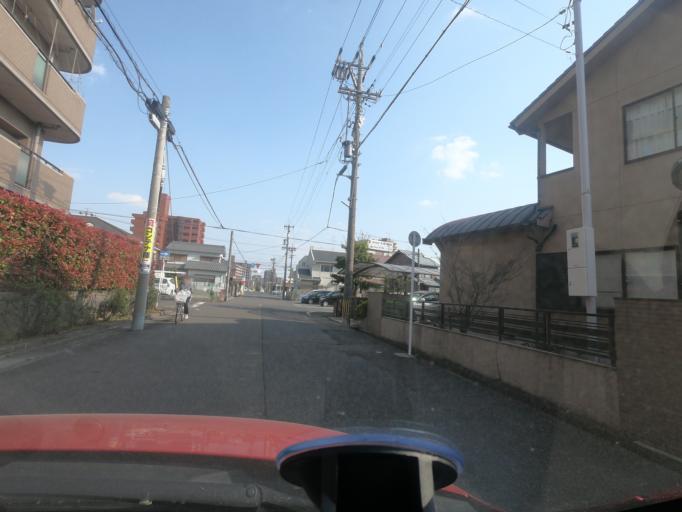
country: JP
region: Aichi
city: Kasugai
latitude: 35.2517
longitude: 136.9792
